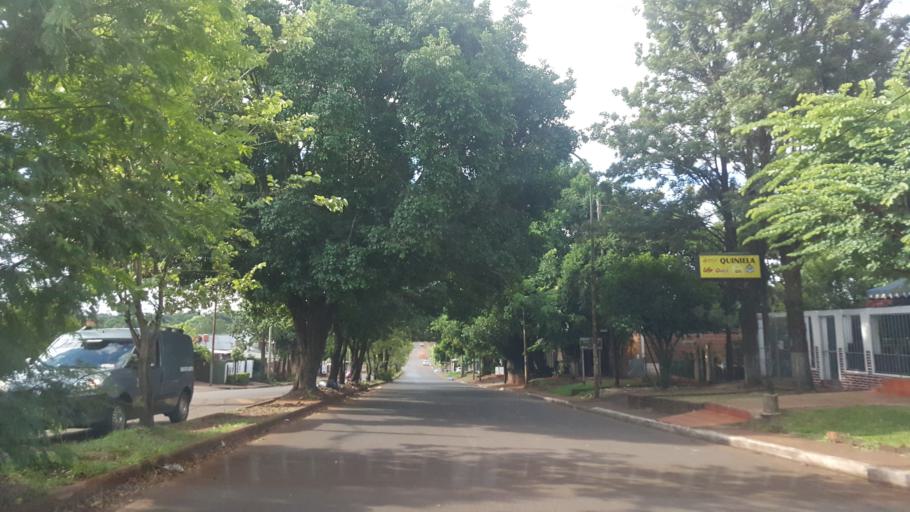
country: AR
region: Misiones
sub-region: Departamento de Capital
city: Posadas
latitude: -27.3958
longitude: -55.9356
